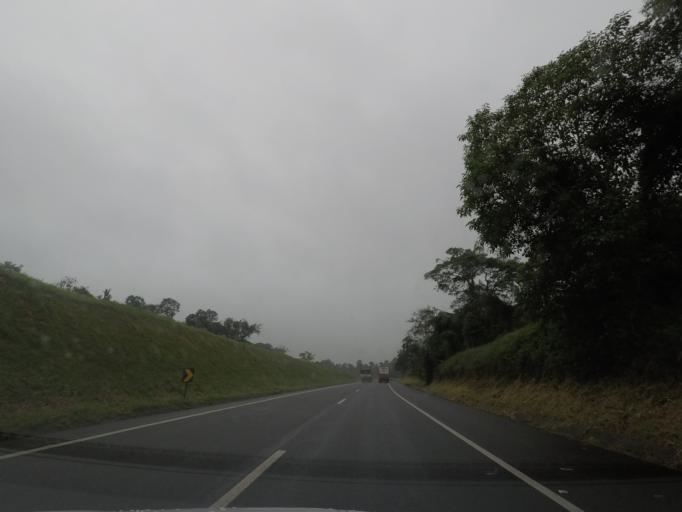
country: BR
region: Sao Paulo
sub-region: Cajati
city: Cajati
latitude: -24.9696
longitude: -48.3641
